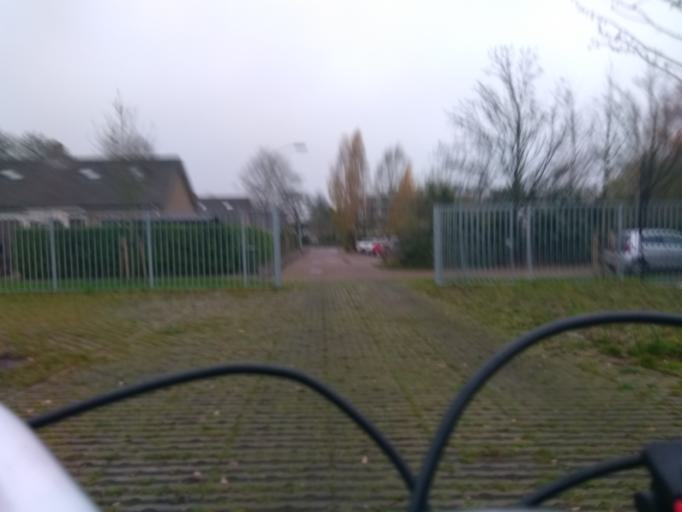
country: NL
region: Drenthe
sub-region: Gemeente Assen
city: Assen
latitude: 53.0055
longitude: 6.5591
